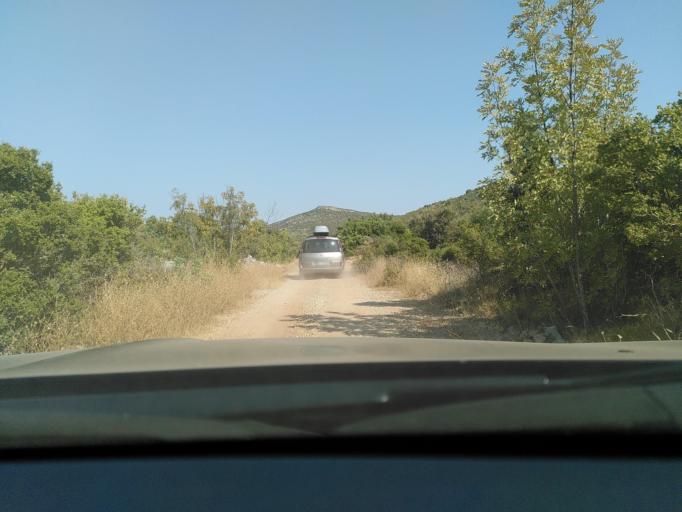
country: HR
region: Splitsko-Dalmatinska
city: Stari Grad
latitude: 43.1611
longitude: 16.5551
